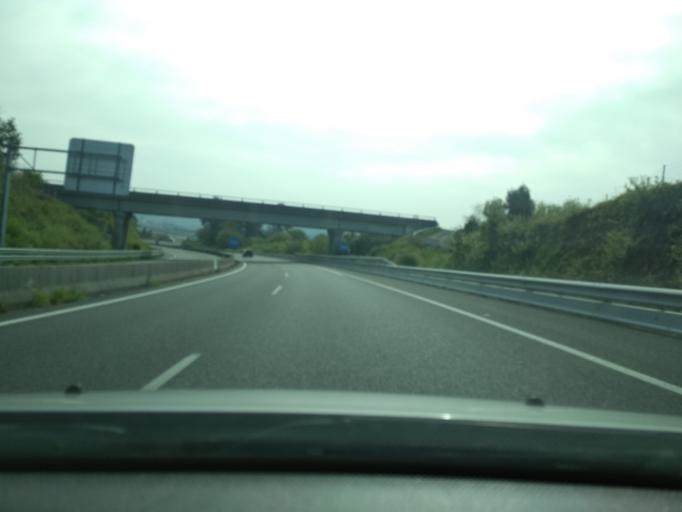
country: ES
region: Galicia
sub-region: Provincia da Coruna
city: Rianxo
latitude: 42.6688
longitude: -8.8250
